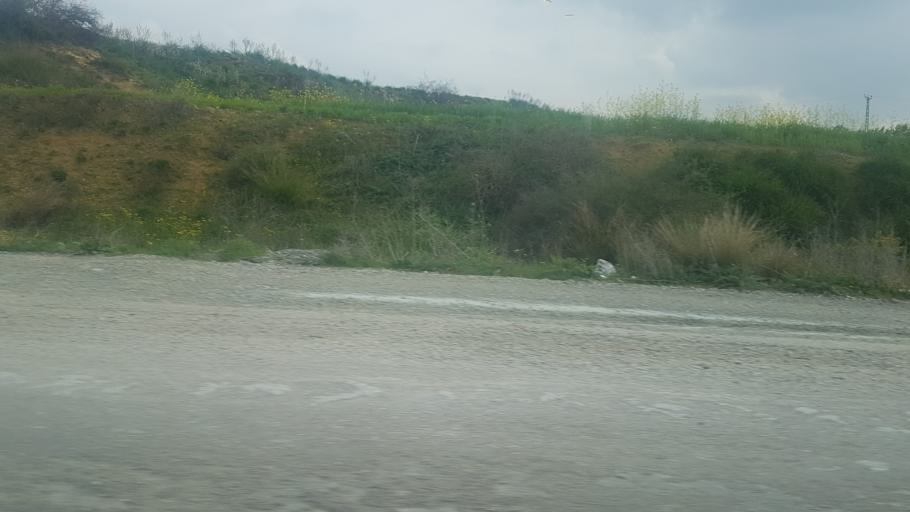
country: TR
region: Adana
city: Seyhan
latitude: 37.0435
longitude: 35.1847
